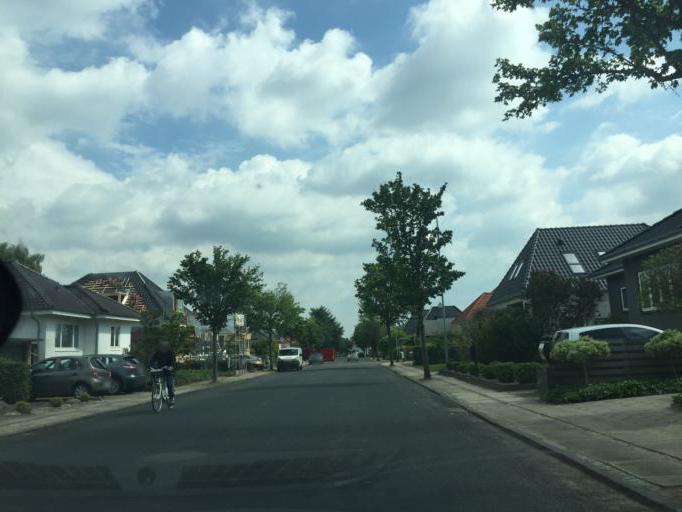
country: DK
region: South Denmark
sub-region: Odense Kommune
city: Odense
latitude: 55.3759
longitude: 10.3581
